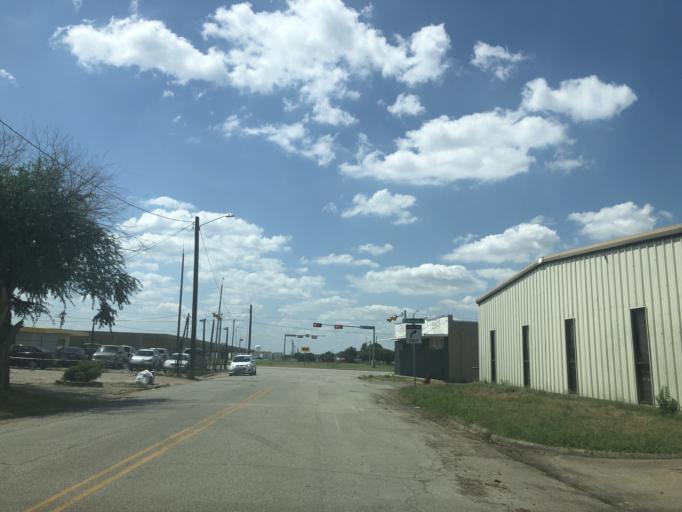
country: US
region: Texas
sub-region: Dallas County
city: Grand Prairie
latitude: 32.7420
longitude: -97.0231
